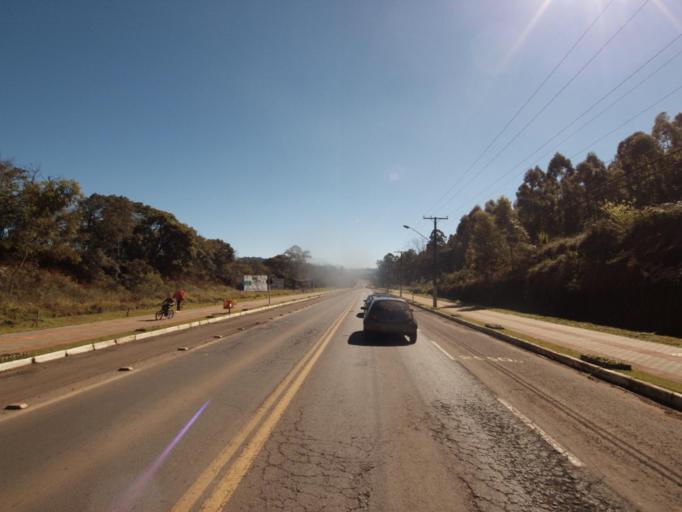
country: AR
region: Misiones
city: Bernardo de Irigoyen
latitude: -26.7570
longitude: -53.5046
